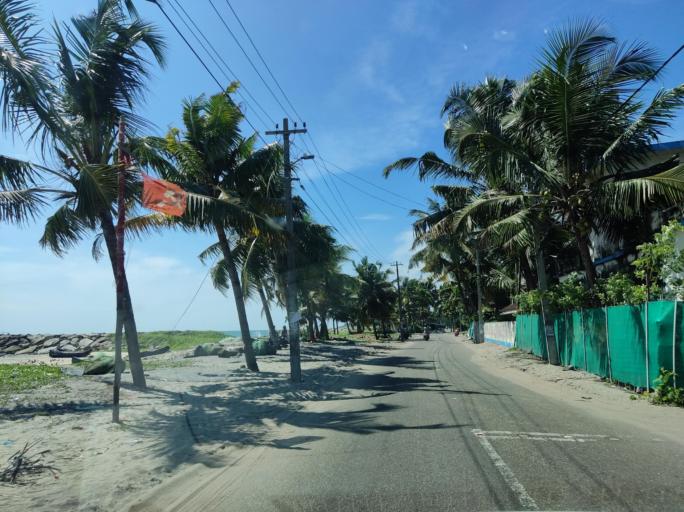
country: IN
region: Kerala
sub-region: Alappuzha
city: Kayankulam
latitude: 9.2008
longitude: 76.4338
